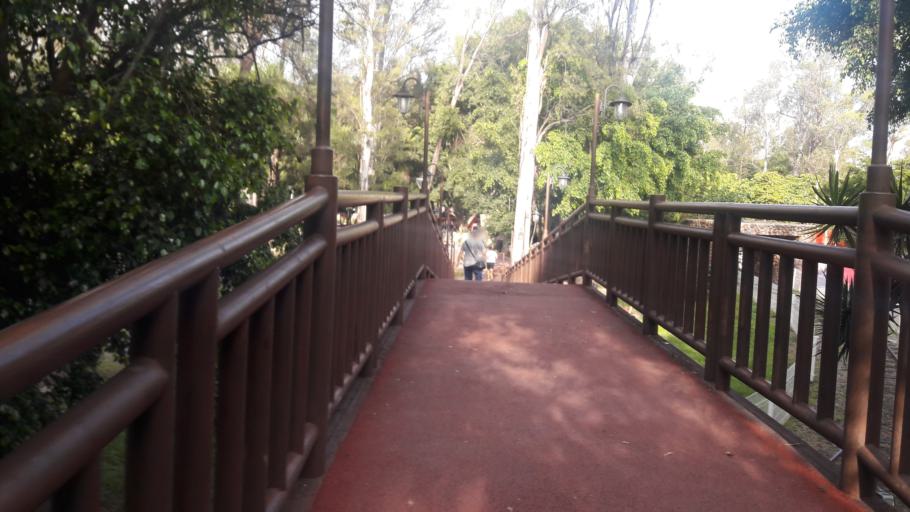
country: MX
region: Nayarit
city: Tepic
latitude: 21.5024
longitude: -104.9012
